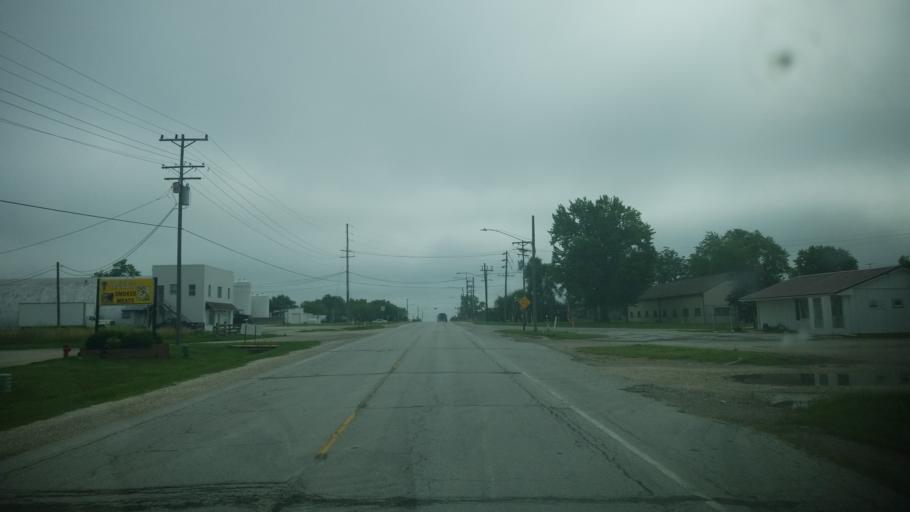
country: US
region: Missouri
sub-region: Pike County
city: Bowling Green
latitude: 39.3475
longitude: -91.2097
